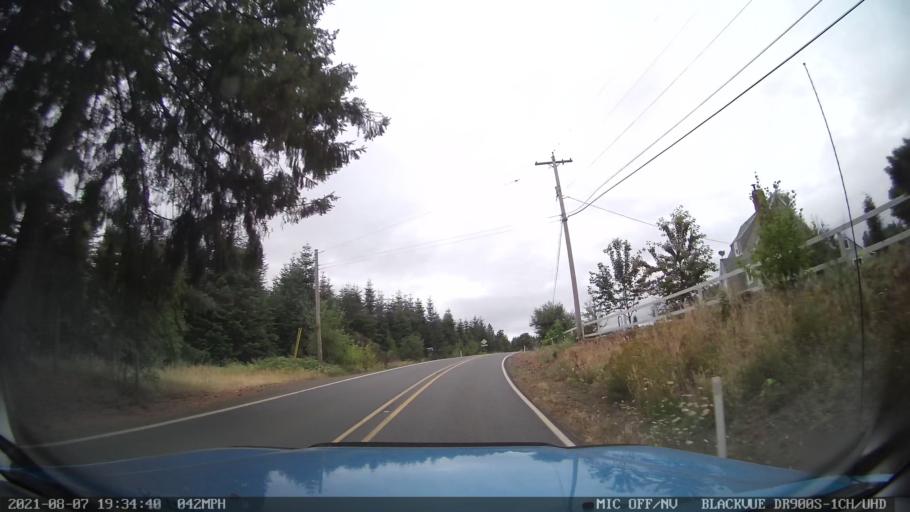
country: US
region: Oregon
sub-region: Linn County
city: Lyons
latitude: 44.9202
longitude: -122.6566
